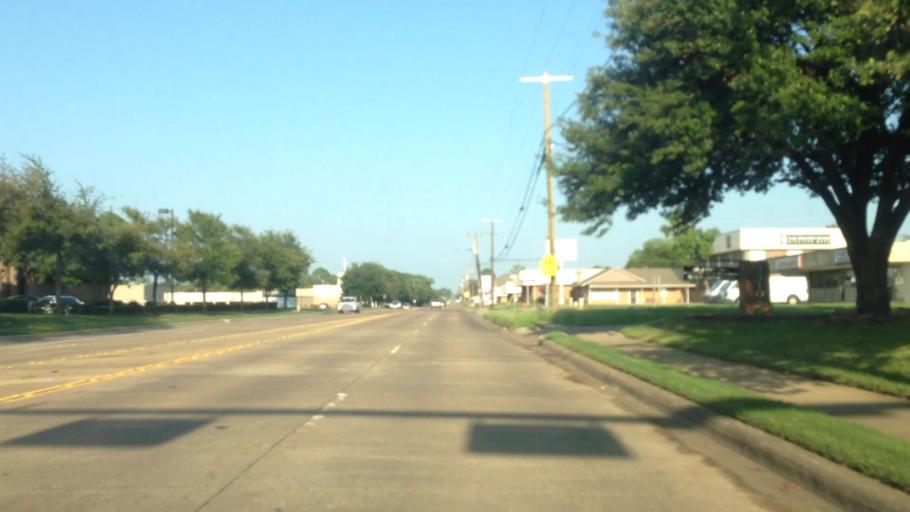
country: US
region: Texas
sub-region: Tarrant County
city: Pantego
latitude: 32.7214
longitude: -97.1610
